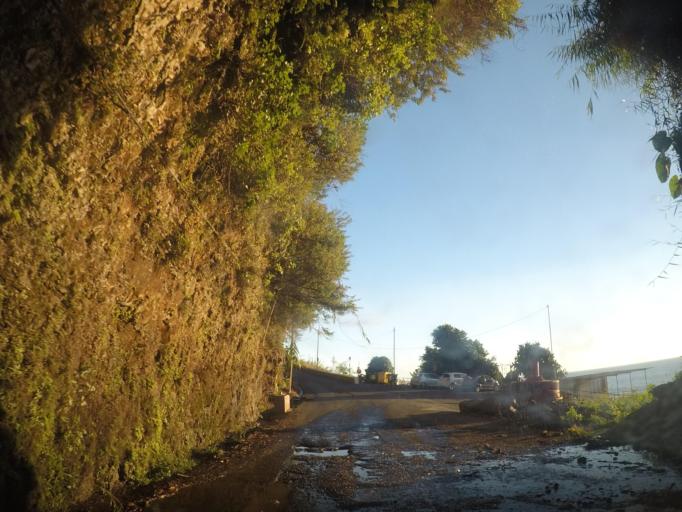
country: PT
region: Madeira
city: Ponta do Sol
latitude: 32.6929
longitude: -17.1176
